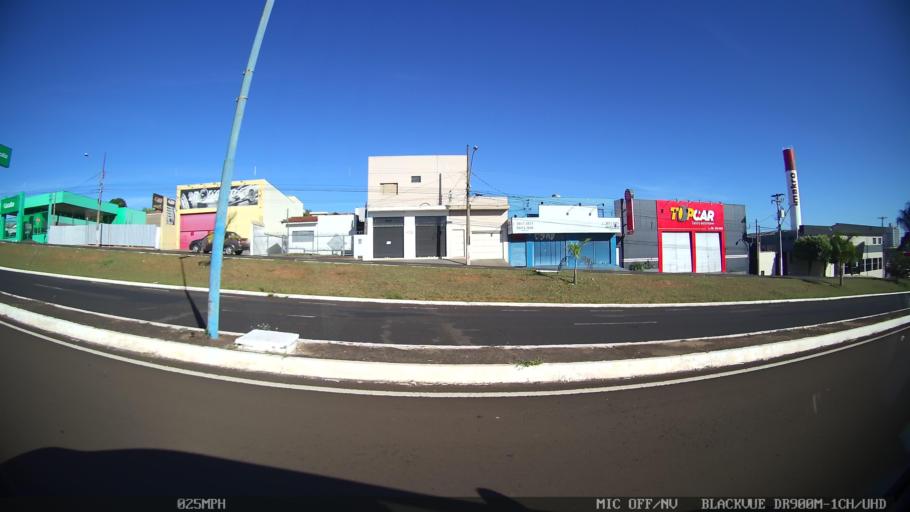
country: BR
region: Sao Paulo
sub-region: Franca
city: Franca
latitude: -20.5556
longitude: -47.3960
